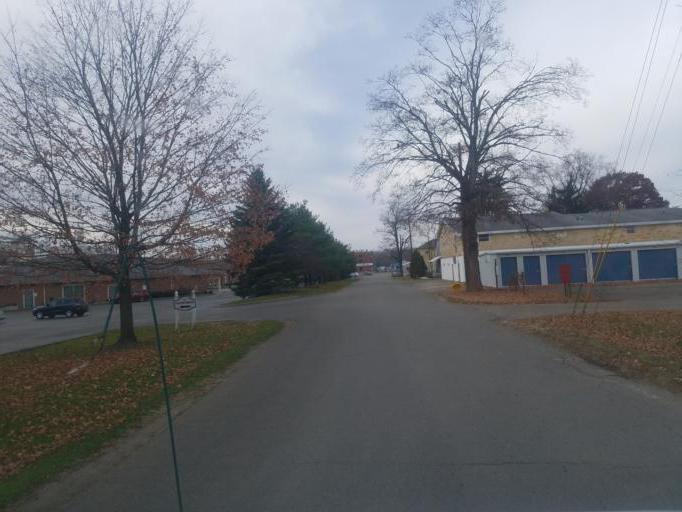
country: US
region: Ohio
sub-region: Knox County
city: Mount Vernon
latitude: 40.3897
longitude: -82.4820
